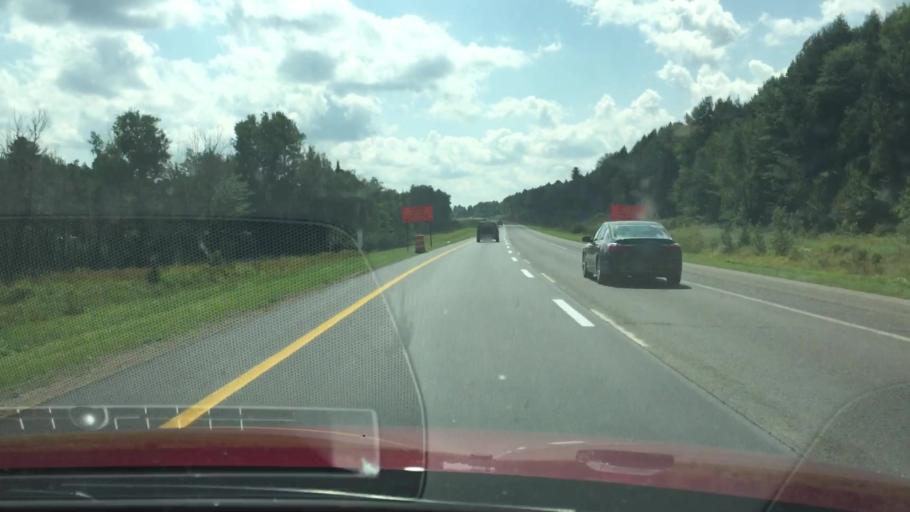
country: US
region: Maine
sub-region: Penobscot County
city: Medway
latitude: 45.6371
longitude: -68.5015
